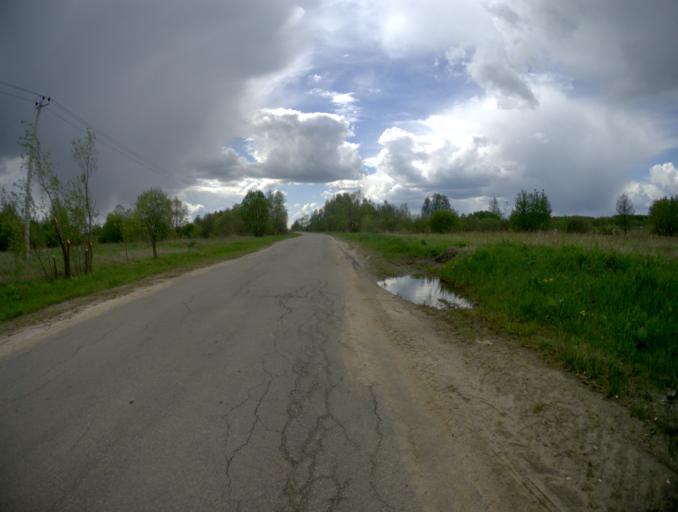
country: RU
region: Vladimir
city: Velikodvorskiy
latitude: 55.2642
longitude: 40.7923
